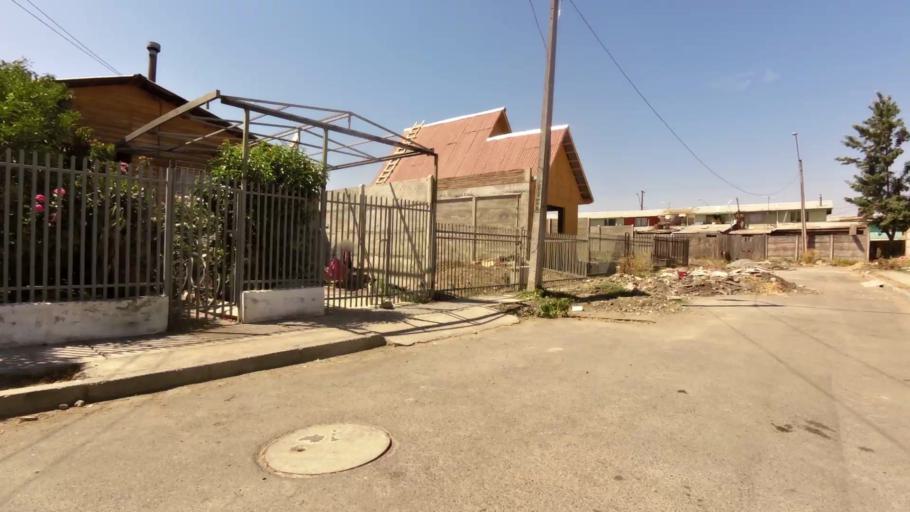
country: CL
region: Maule
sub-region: Provincia de Curico
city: Curico
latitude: -34.9641
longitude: -71.2353
